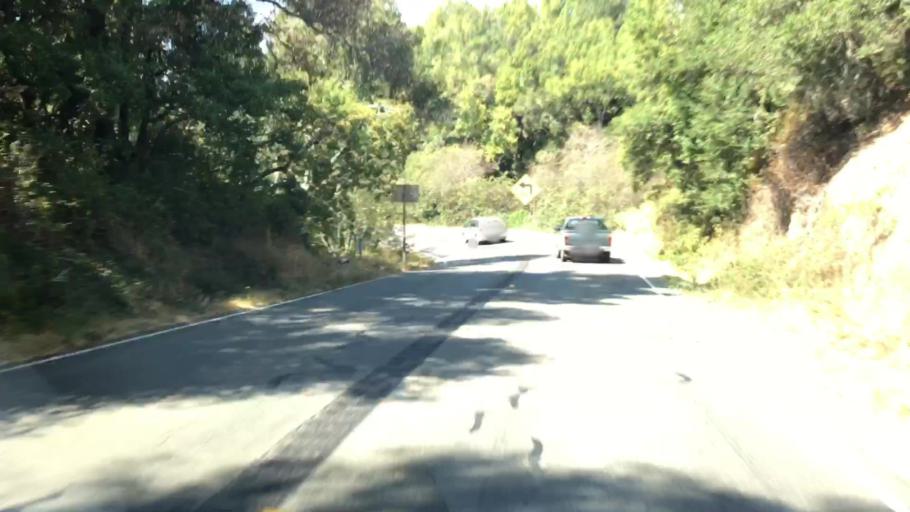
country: US
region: California
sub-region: Marin County
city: Lagunitas-Forest Knolls
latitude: 38.0241
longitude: -122.7748
